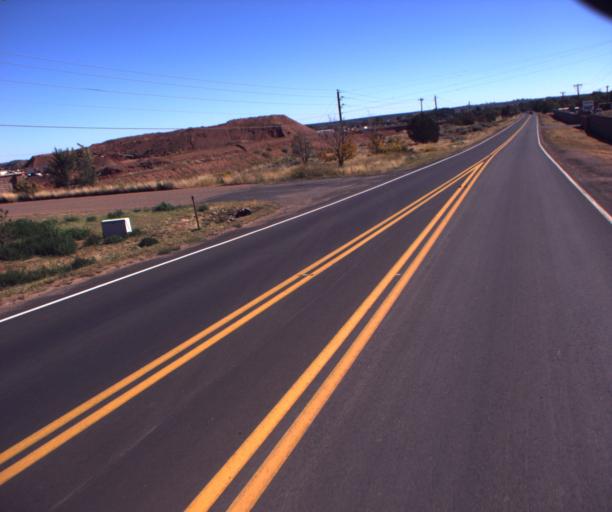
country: US
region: Arizona
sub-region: Navajo County
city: Snowflake
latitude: 34.5132
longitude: -110.0954
